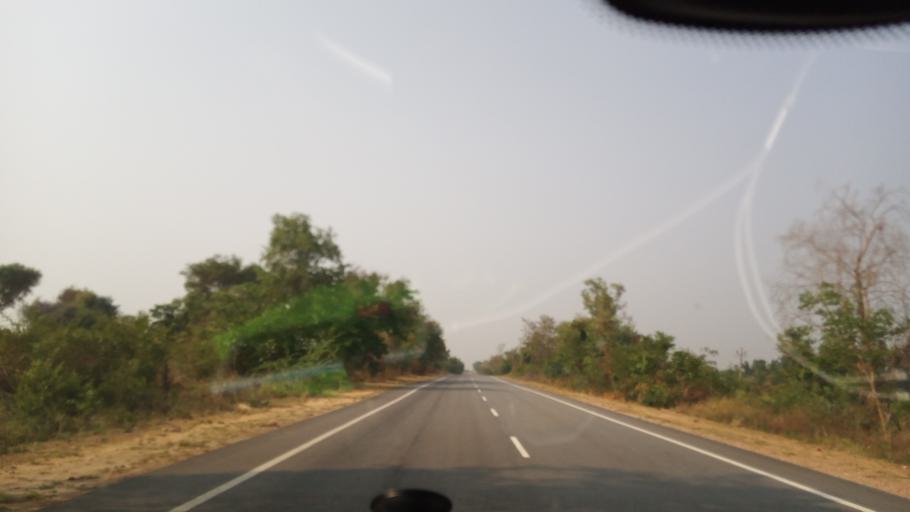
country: IN
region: Karnataka
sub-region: Mandya
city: Belluru
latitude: 12.9258
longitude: 76.7489
